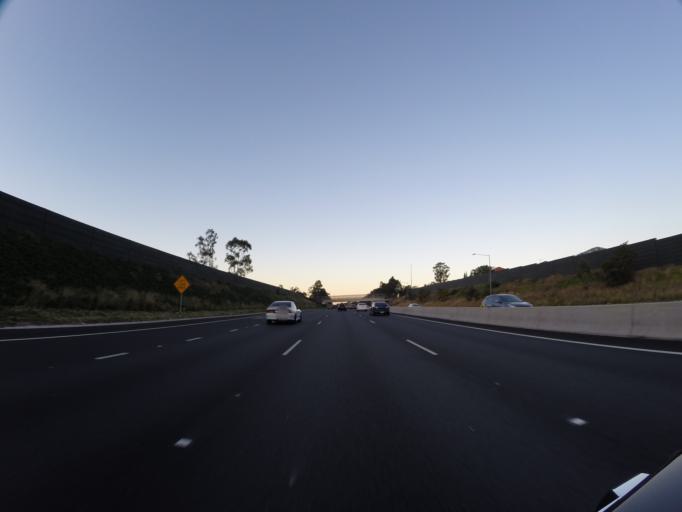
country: AU
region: New South Wales
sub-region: Campbelltown Municipality
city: Glenfield
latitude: -33.9489
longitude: 150.8885
